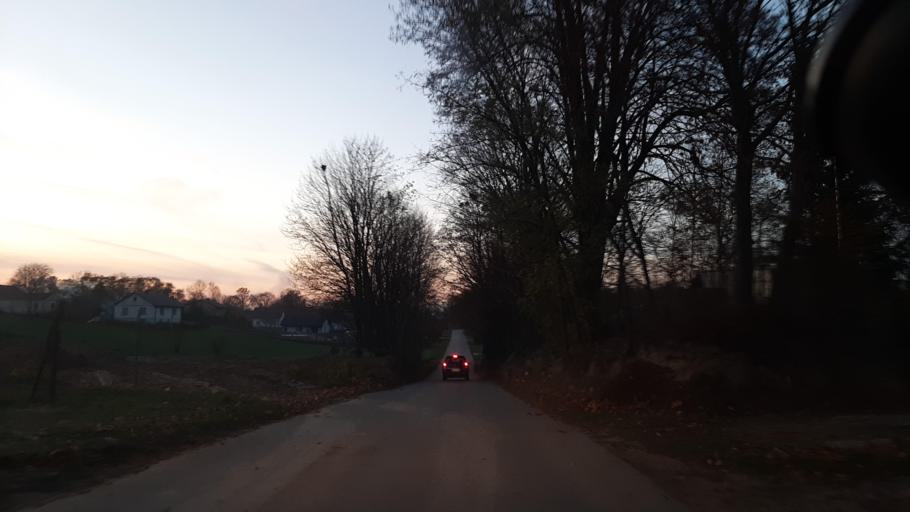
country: PL
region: Lublin Voivodeship
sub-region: Powiat lubelski
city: Jastkow
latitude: 51.3385
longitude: 22.4225
